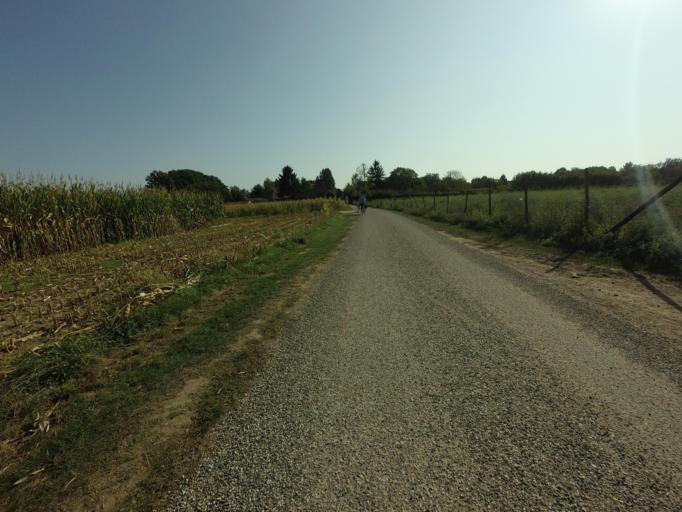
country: NL
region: Limburg
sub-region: Gemeente Maasgouw
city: Maasbracht
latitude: 51.1506
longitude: 5.9015
